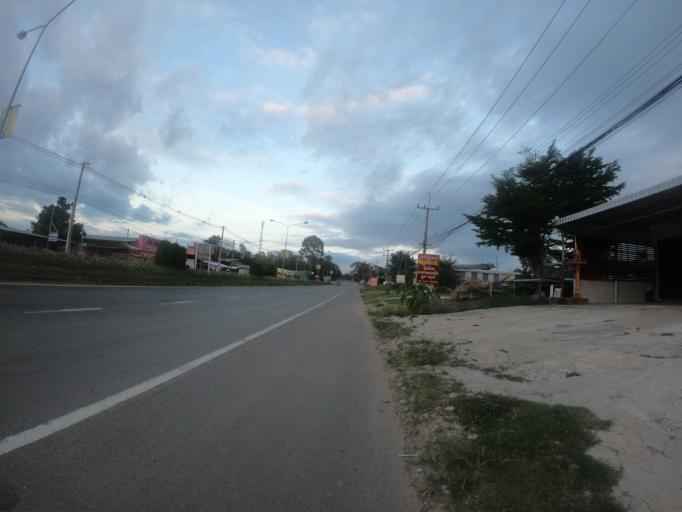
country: TH
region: Surin
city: Kap Choeng
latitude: 14.4524
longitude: 103.6933
